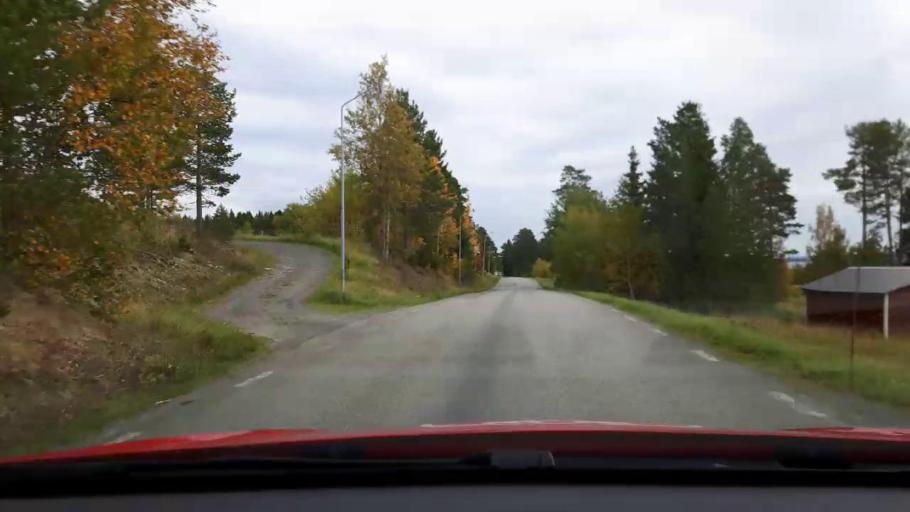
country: SE
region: Jaemtland
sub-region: Krokoms Kommun
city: Valla
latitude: 63.2578
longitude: 14.0171
